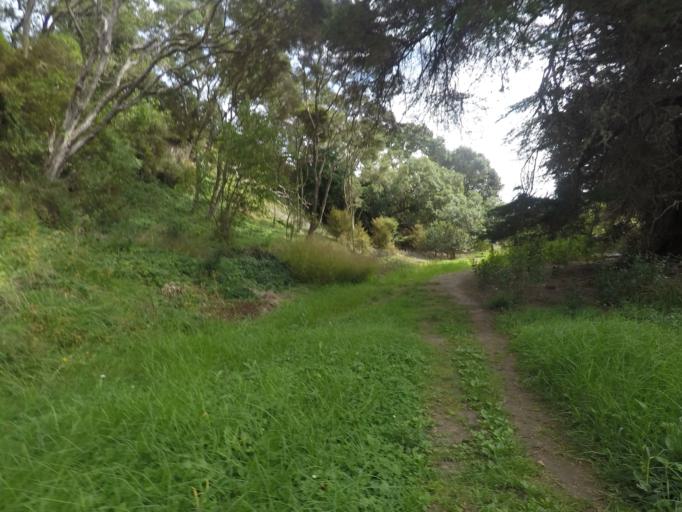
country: NZ
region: Auckland
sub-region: Auckland
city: Rothesay Bay
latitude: -36.6447
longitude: 174.7240
